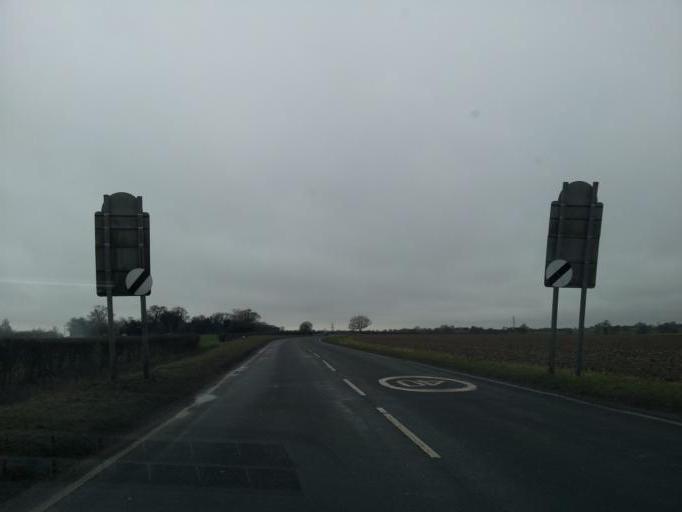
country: GB
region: England
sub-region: Essex
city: Mistley
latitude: 51.9108
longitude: 1.0824
